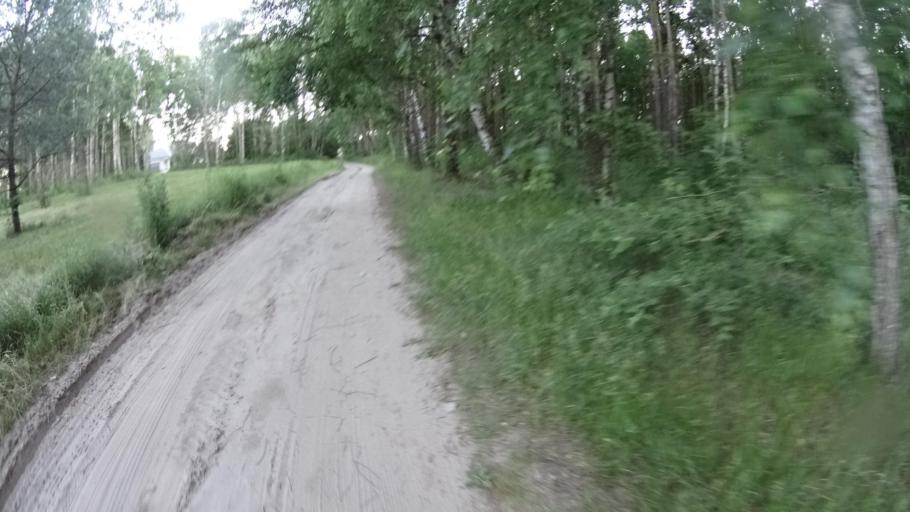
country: PL
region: Masovian Voivodeship
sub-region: Powiat warszawski zachodni
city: Jozefow
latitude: 52.2697
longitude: 20.6947
